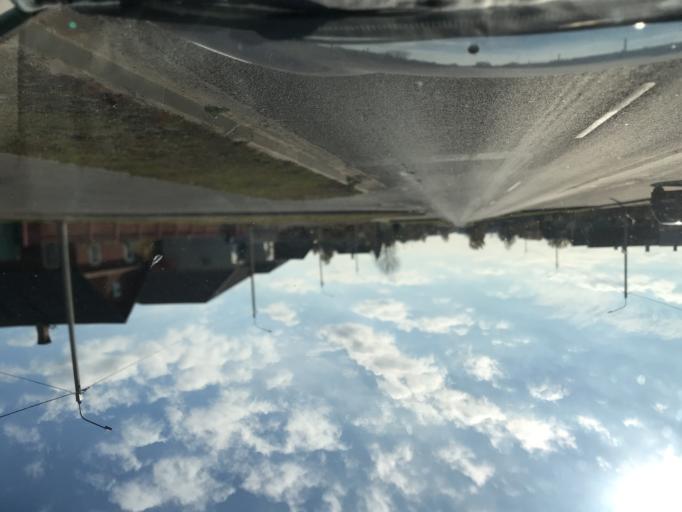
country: LT
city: Salcininkai
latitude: 54.2499
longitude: 25.3560
